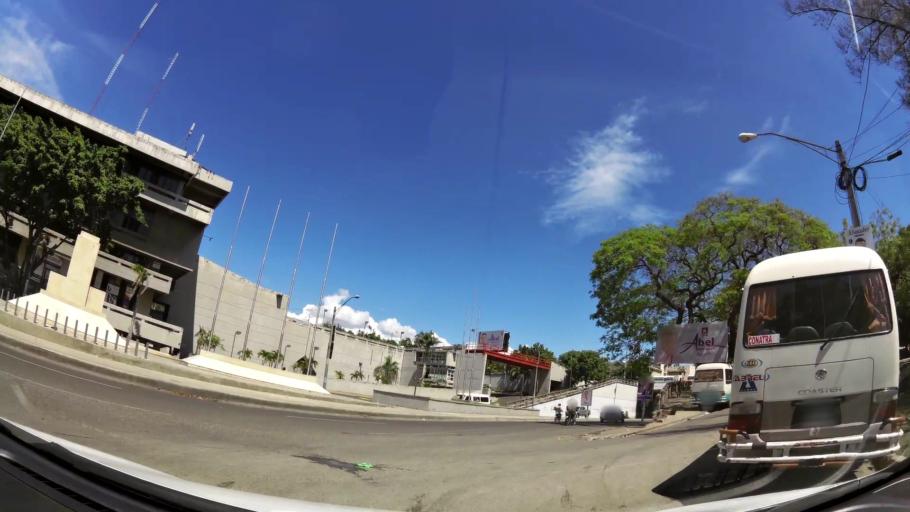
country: DO
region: Santiago
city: Santiago de los Caballeros
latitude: 19.4553
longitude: -70.7062
